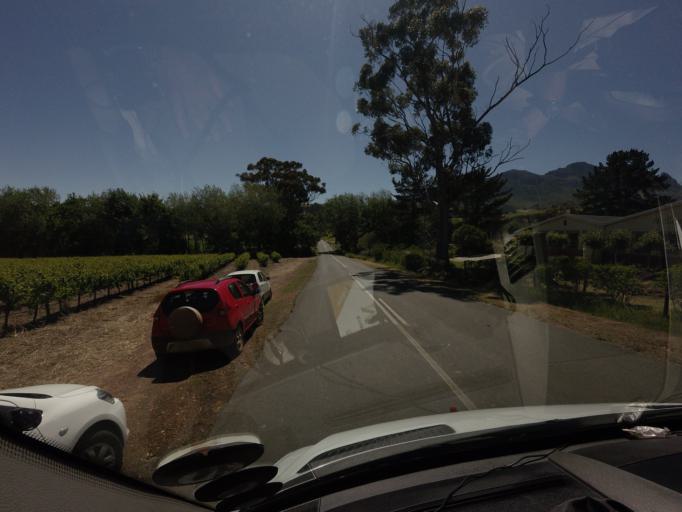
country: ZA
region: Western Cape
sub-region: Cape Winelands District Municipality
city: Stellenbosch
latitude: -33.8751
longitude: 18.8590
